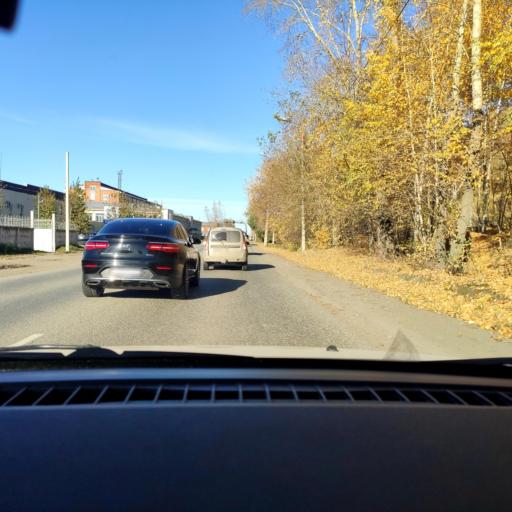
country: RU
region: Perm
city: Perm
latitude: 58.0913
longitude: 56.3539
